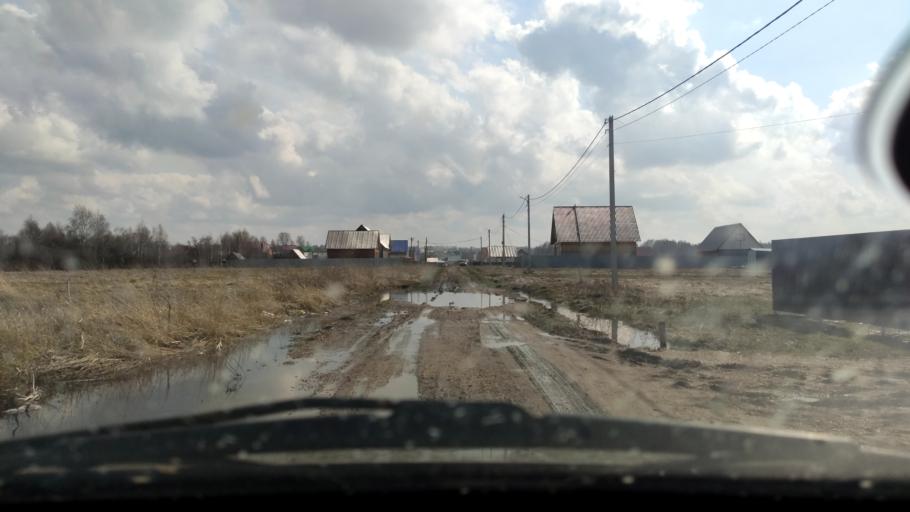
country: RU
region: Bashkortostan
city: Iglino
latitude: 54.8273
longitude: 56.3700
